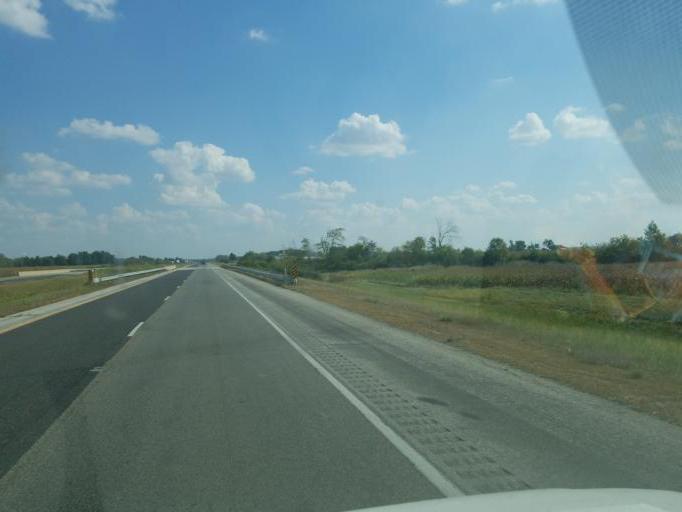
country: US
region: Indiana
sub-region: Allen County
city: Monroeville
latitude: 41.0097
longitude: -84.8515
